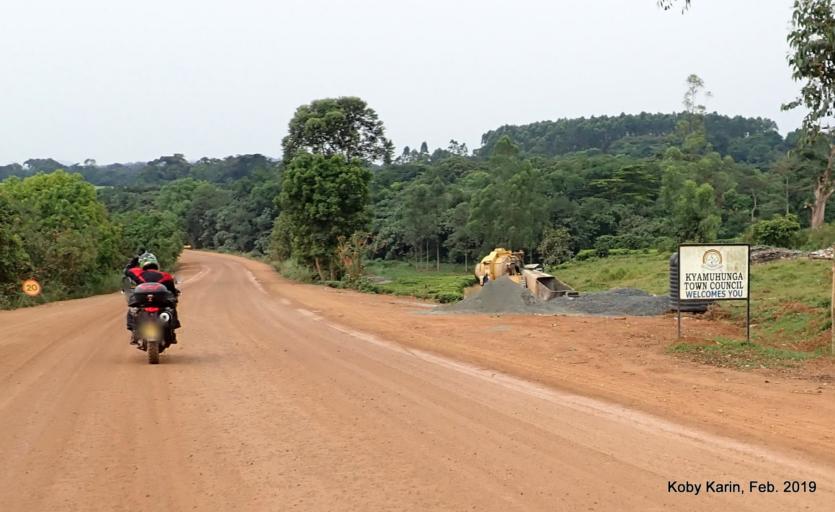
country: UG
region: Western Region
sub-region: Rubirizi District
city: Rubirizi
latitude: -0.3805
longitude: 30.1138
